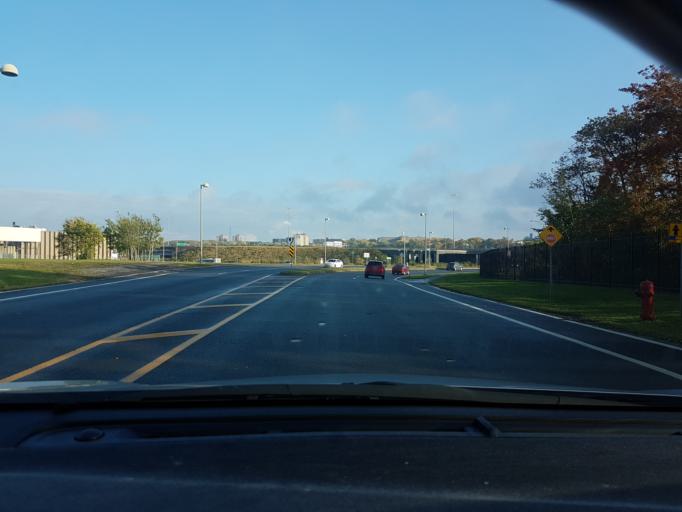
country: CA
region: Quebec
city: L'Ancienne-Lorette
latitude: 46.7961
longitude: -71.2936
